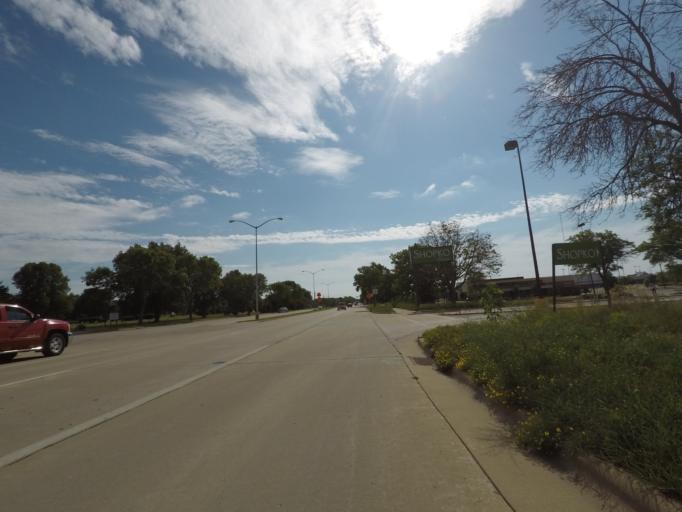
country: US
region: Wisconsin
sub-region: Dane County
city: Middleton
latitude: 43.0605
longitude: -89.5105
